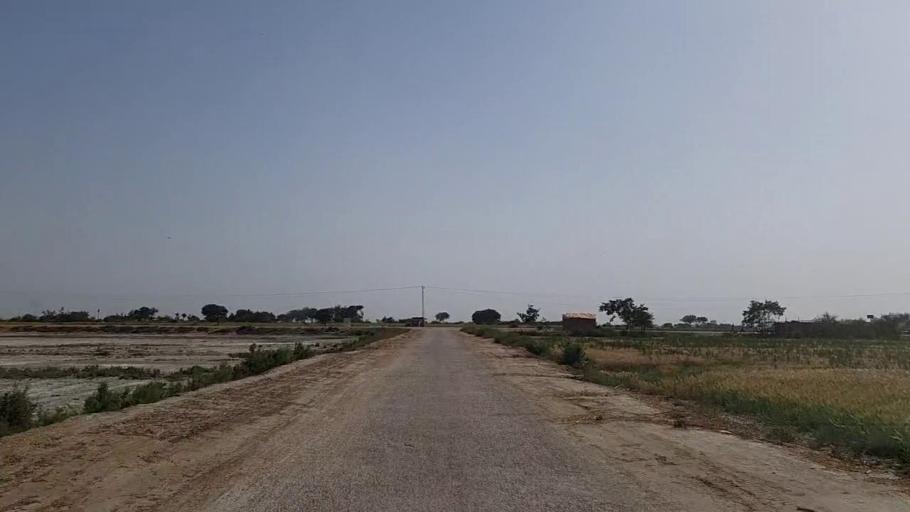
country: PK
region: Sindh
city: Jati
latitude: 24.3516
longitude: 68.2761
